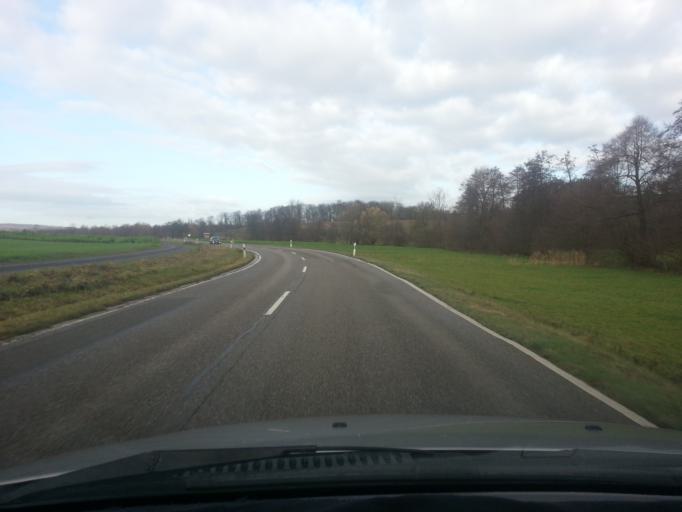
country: DE
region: Baden-Wuerttemberg
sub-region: Regierungsbezirk Stuttgart
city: Eppingen
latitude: 49.1512
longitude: 8.8927
